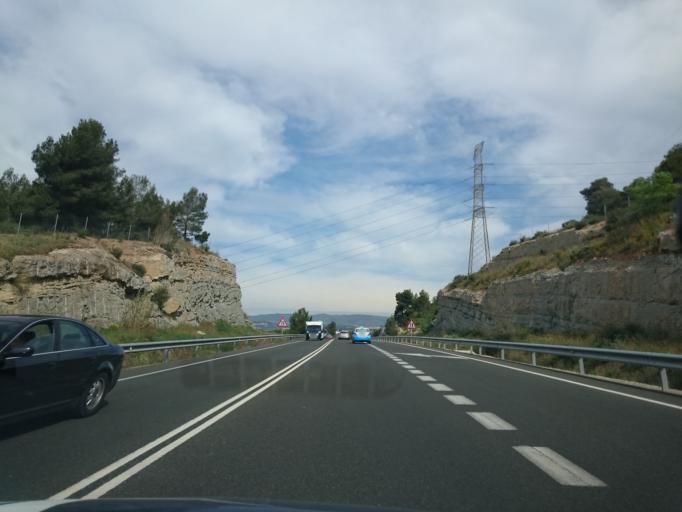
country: ES
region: Catalonia
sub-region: Provincia de Barcelona
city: La Pobla de Claramunt
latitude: 41.5648
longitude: 1.6780
